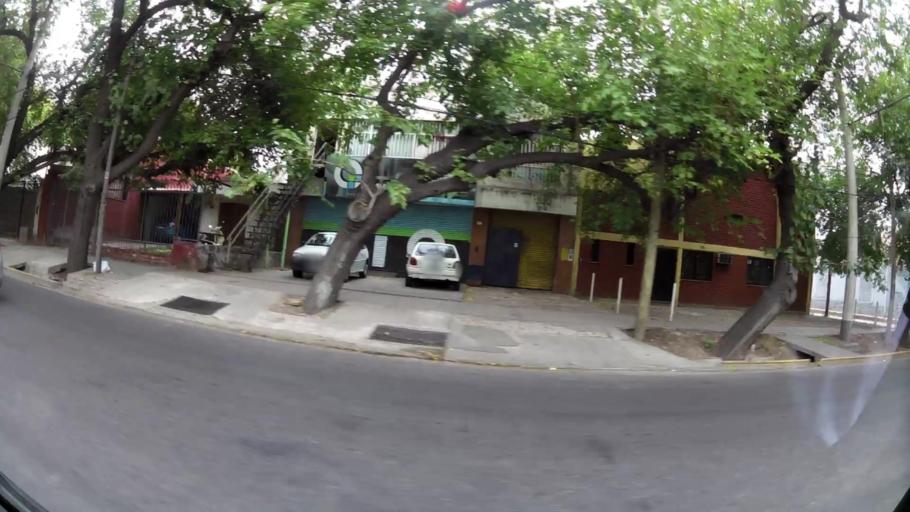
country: AR
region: Mendoza
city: Mendoza
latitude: -32.8785
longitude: -68.8456
